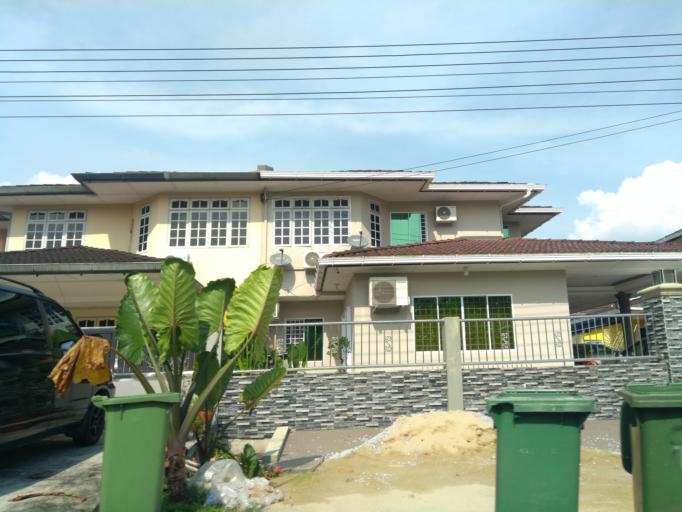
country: MY
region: Sarawak
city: Kuching
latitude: 1.5760
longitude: 110.2937
